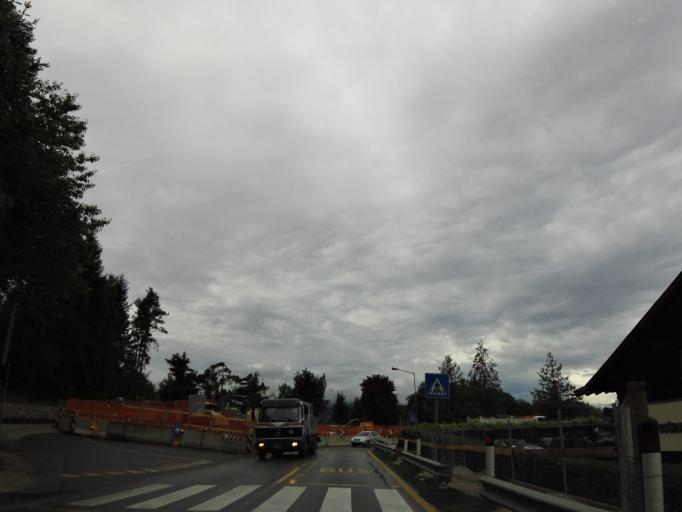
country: IT
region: Trentino-Alto Adige
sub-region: Bolzano
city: Fie Allo Sciliar
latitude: 46.5255
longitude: 11.5091
